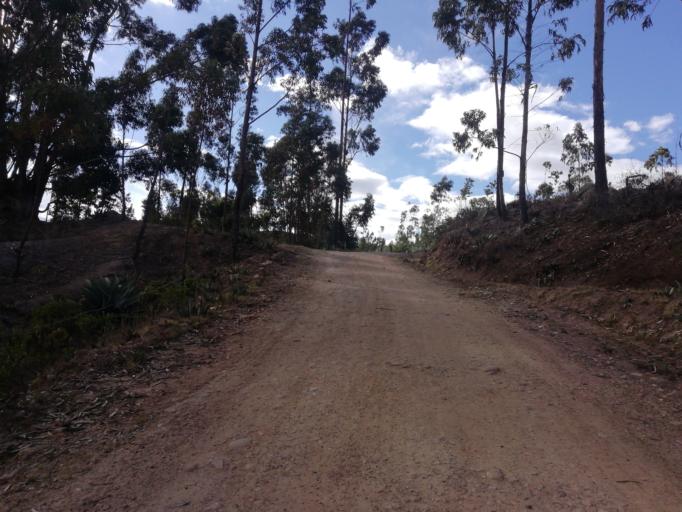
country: CO
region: Boyaca
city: Gameza
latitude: 5.8094
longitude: -72.8127
